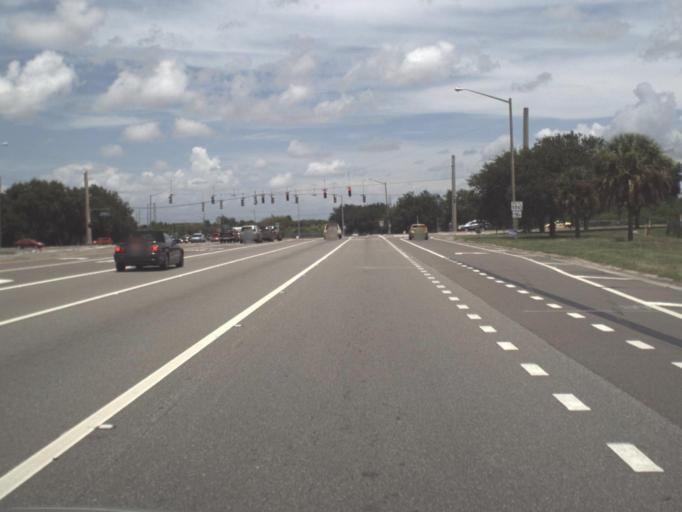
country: US
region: Florida
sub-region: Pinellas County
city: Saint George
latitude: 28.0477
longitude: -82.7091
